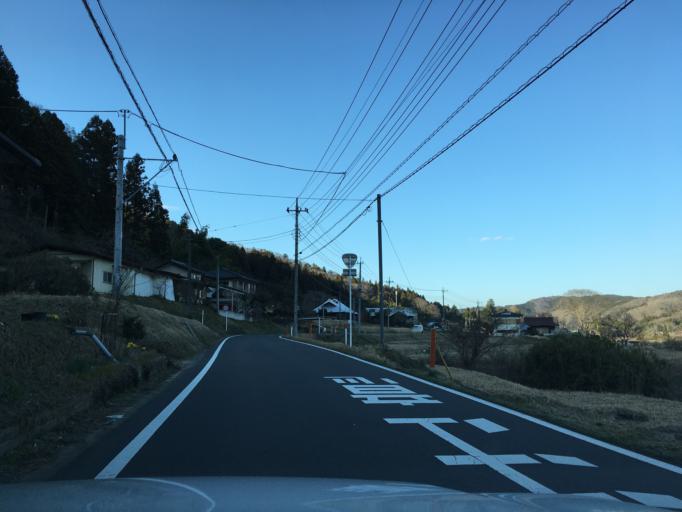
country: JP
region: Tochigi
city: Karasuyama
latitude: 36.7737
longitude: 140.2063
